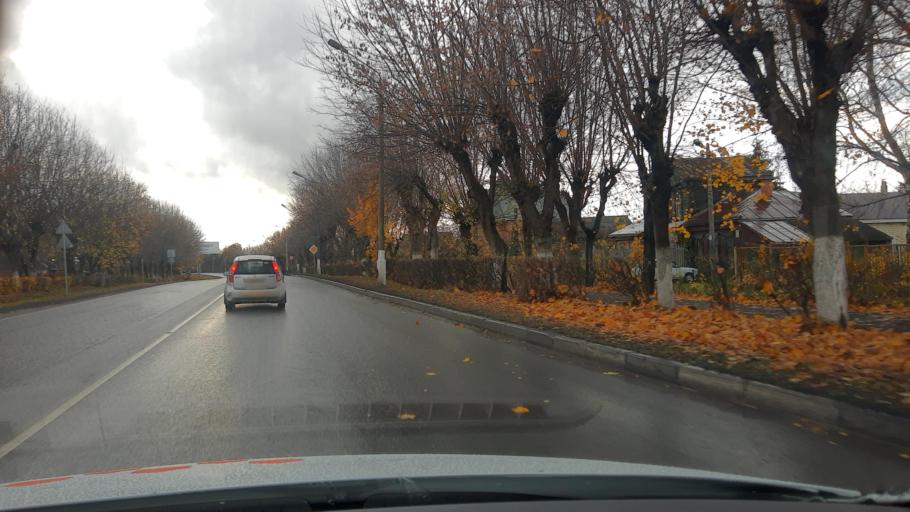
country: RU
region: Moskovskaya
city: Noginsk
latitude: 55.8385
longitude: 38.3934
